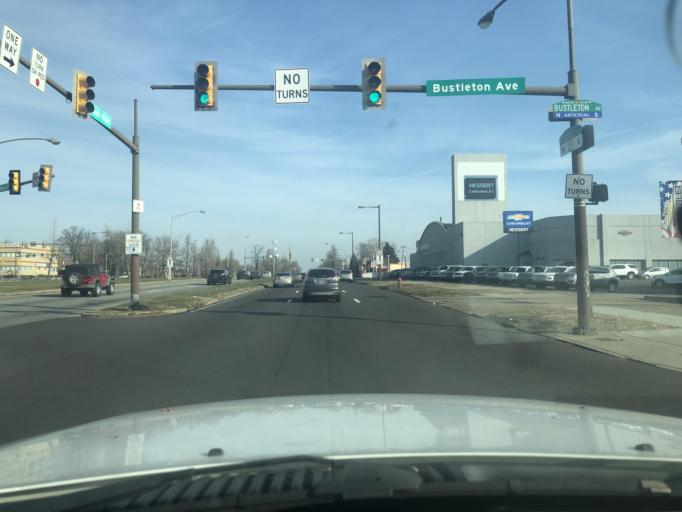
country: US
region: Pennsylvania
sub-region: Montgomery County
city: Rockledge
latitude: 40.0346
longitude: -75.0712
